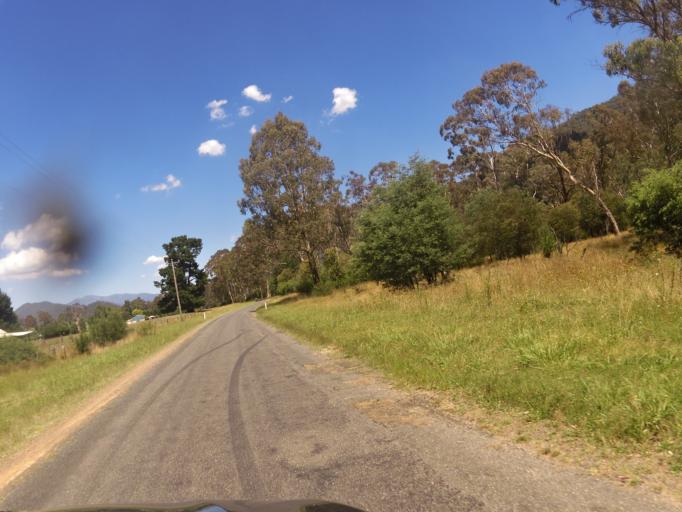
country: AU
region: Victoria
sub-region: Alpine
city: Mount Beauty
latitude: -36.7459
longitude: 147.0189
